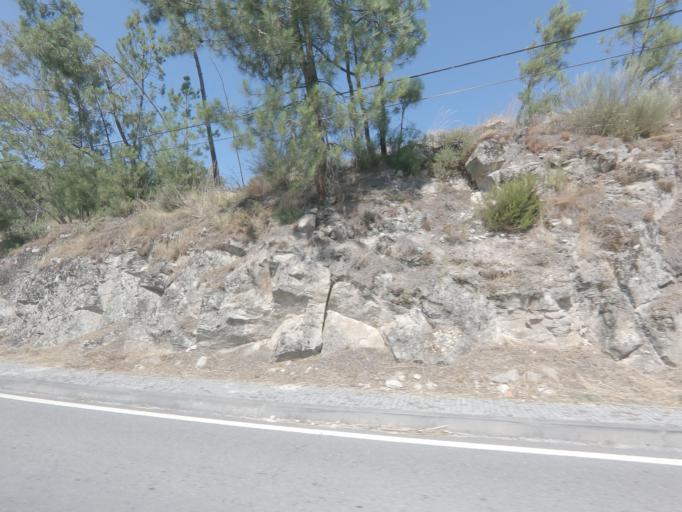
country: PT
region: Viseu
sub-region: Tarouca
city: Tarouca
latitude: 41.0258
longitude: -7.7545
